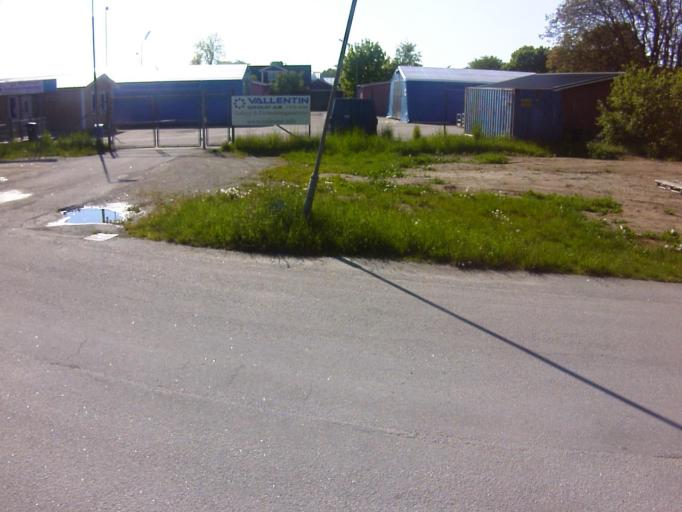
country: SE
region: Blekinge
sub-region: Solvesborgs Kommun
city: Soelvesborg
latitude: 56.0446
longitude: 14.6765
